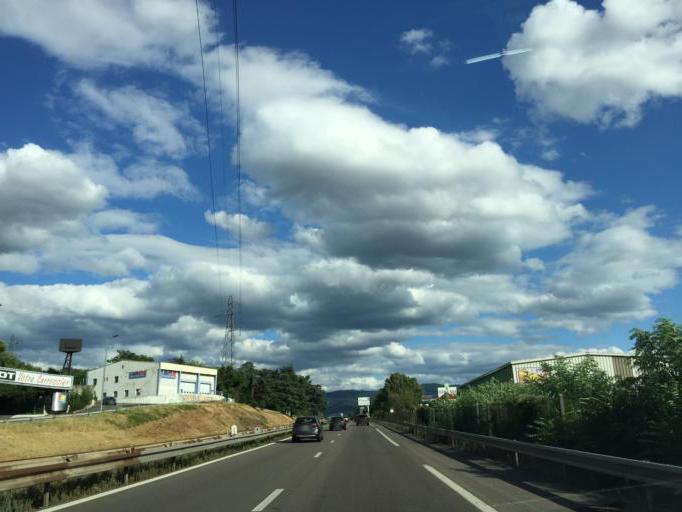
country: FR
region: Rhone-Alpes
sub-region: Departement de la Loire
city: La Tour-en-Jarez
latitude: 45.4616
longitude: 4.4023
